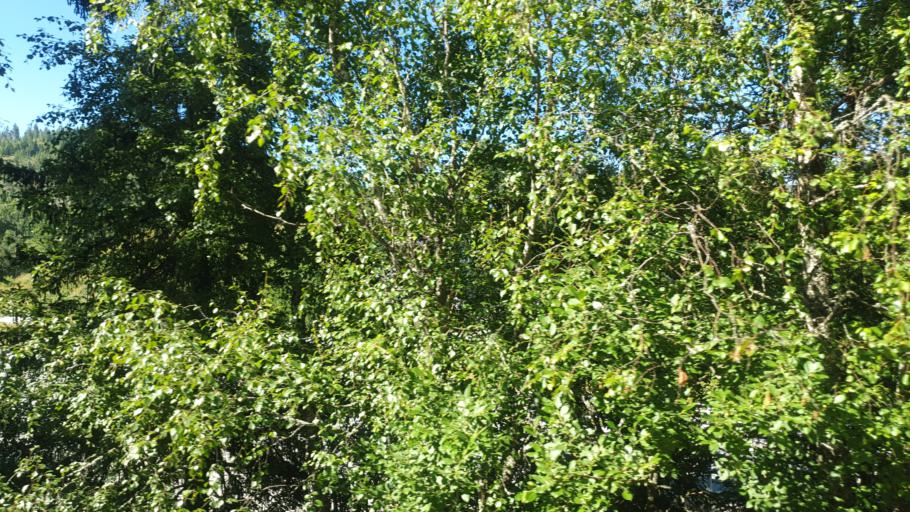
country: NO
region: Sor-Trondelag
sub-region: Meldal
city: Meldal
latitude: 63.1521
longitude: 9.7200
